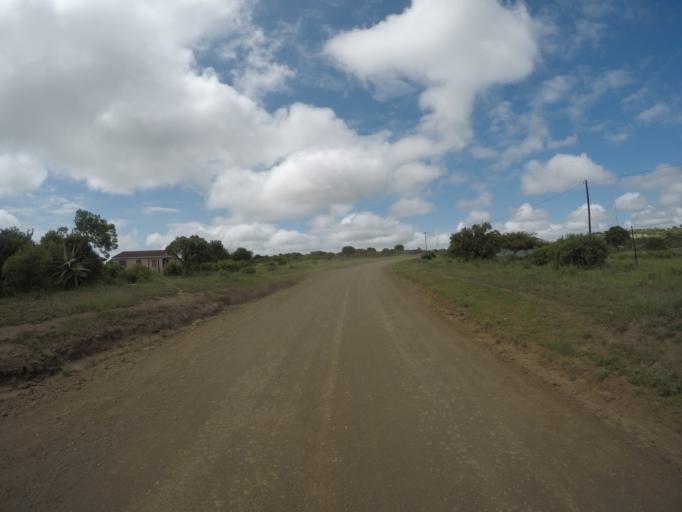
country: ZA
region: KwaZulu-Natal
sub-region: uThungulu District Municipality
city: Empangeni
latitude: -28.5993
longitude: 31.8385
